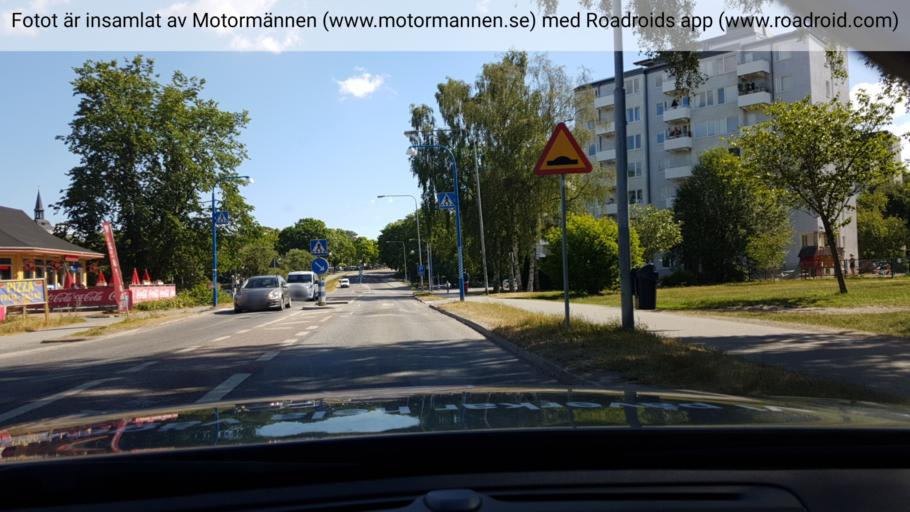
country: SE
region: Stockholm
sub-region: Huddinge Kommun
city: Huddinge
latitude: 59.2378
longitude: 17.9820
